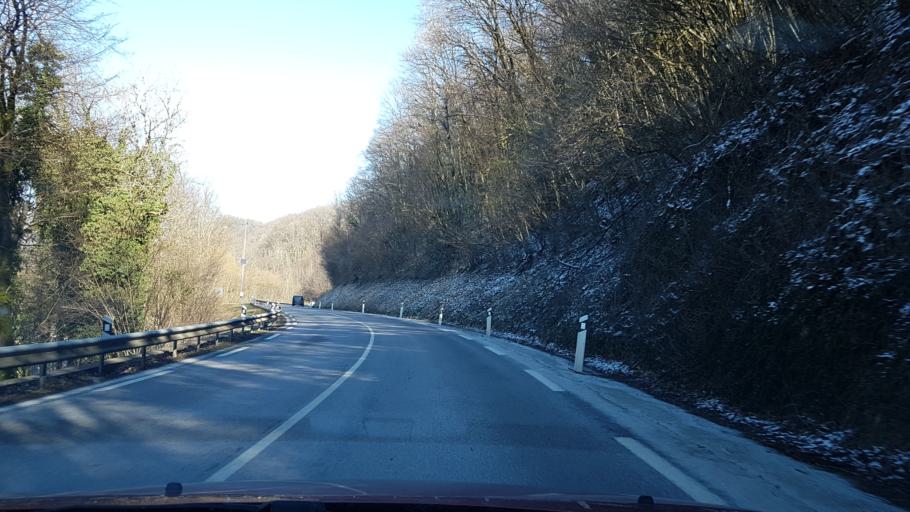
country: FR
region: Franche-Comte
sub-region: Departement du Doubs
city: Avanne-Aveney
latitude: 47.1861
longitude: 5.9648
